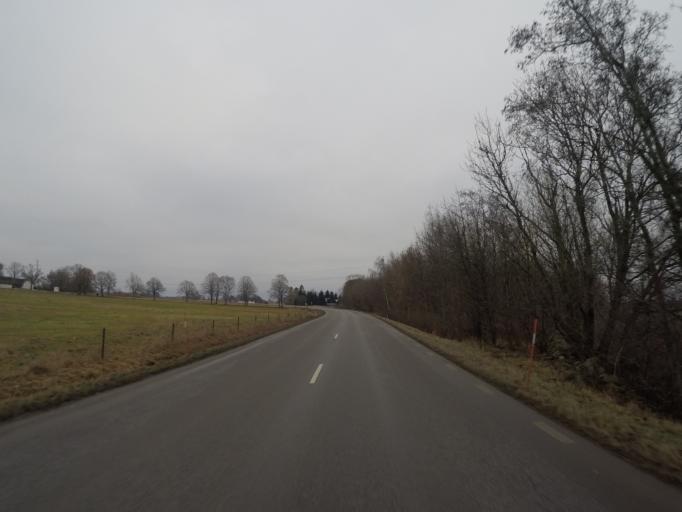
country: SE
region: Skane
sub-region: Hoors Kommun
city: Loberod
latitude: 55.7705
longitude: 13.4411
